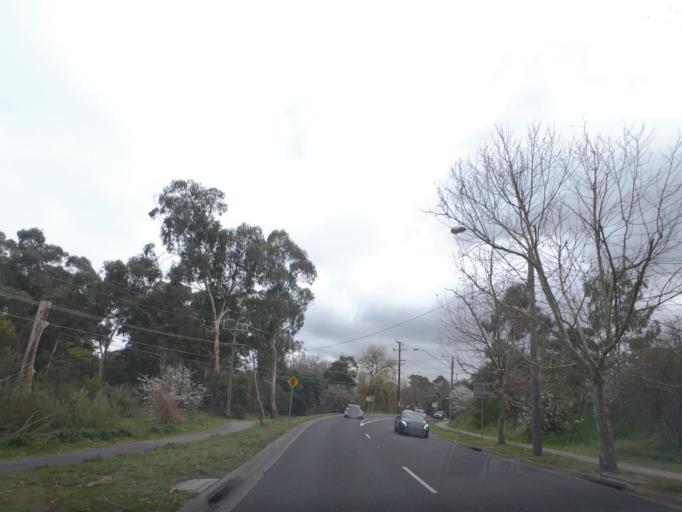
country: AU
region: Victoria
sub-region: Nillumbik
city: Eltham
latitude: -37.7253
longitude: 145.1468
